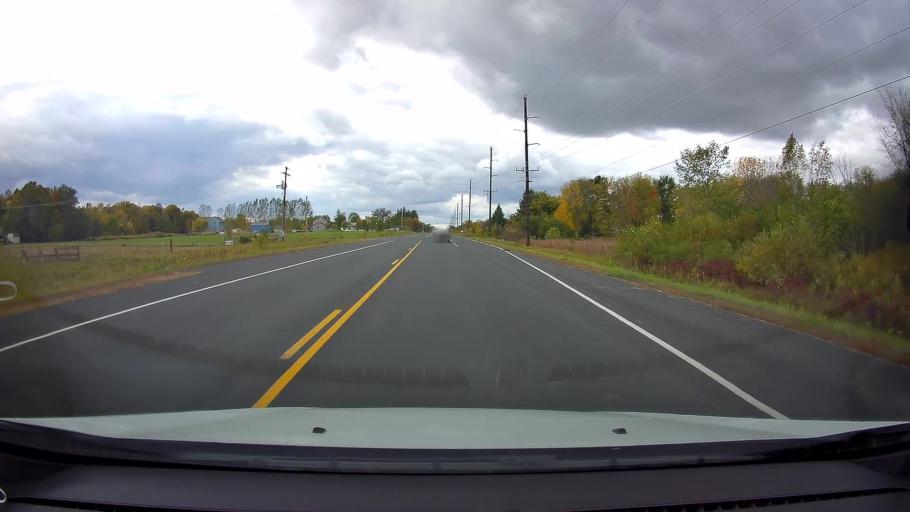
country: US
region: Minnesota
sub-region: Chisago County
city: Shafer
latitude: 45.3972
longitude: -92.7631
